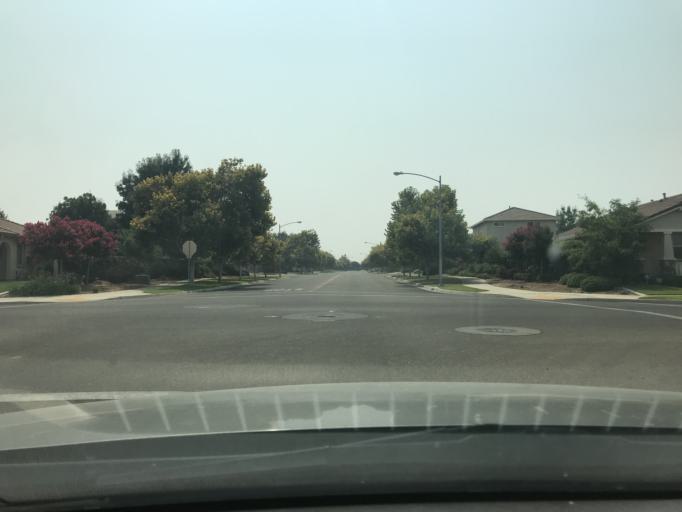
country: US
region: California
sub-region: Merced County
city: Merced
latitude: 37.3559
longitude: -120.4745
